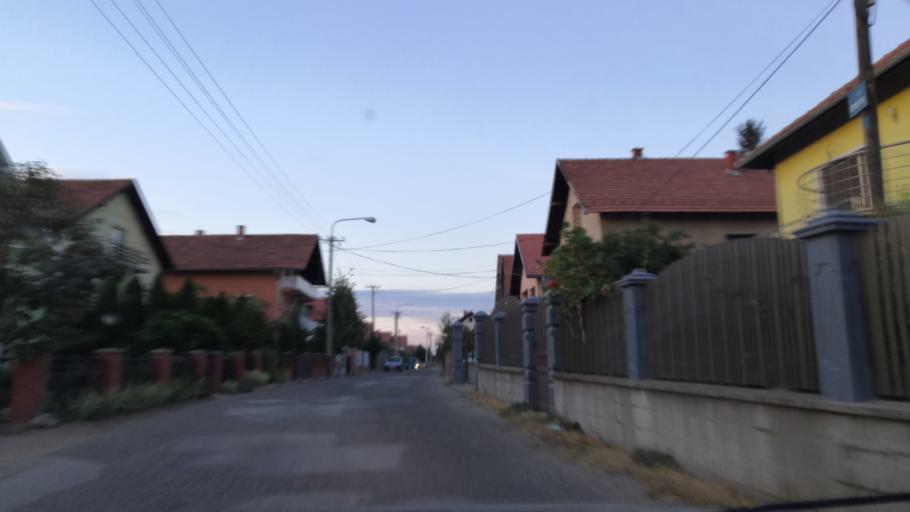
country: RS
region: Central Serbia
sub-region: Borski Okrug
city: Negotin
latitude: 44.2396
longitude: 22.5290
